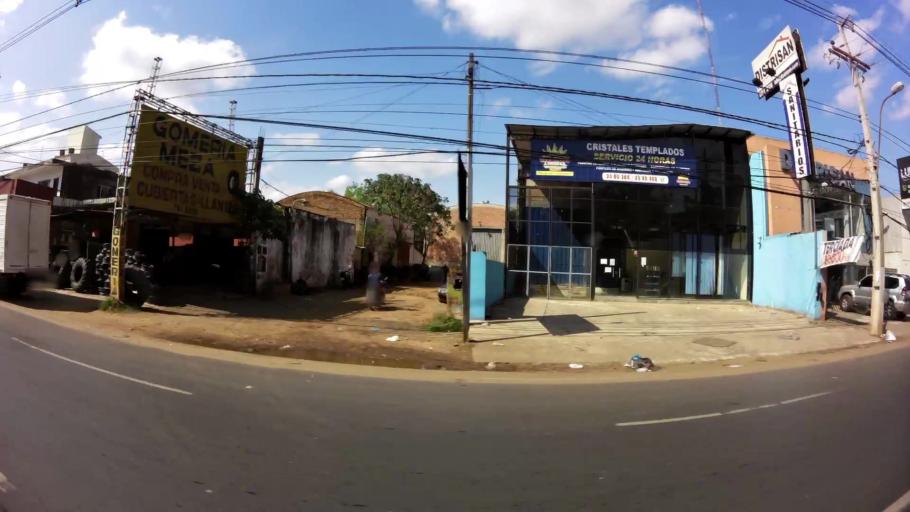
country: PY
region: Central
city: Fernando de la Mora
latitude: -25.3306
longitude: -57.5425
